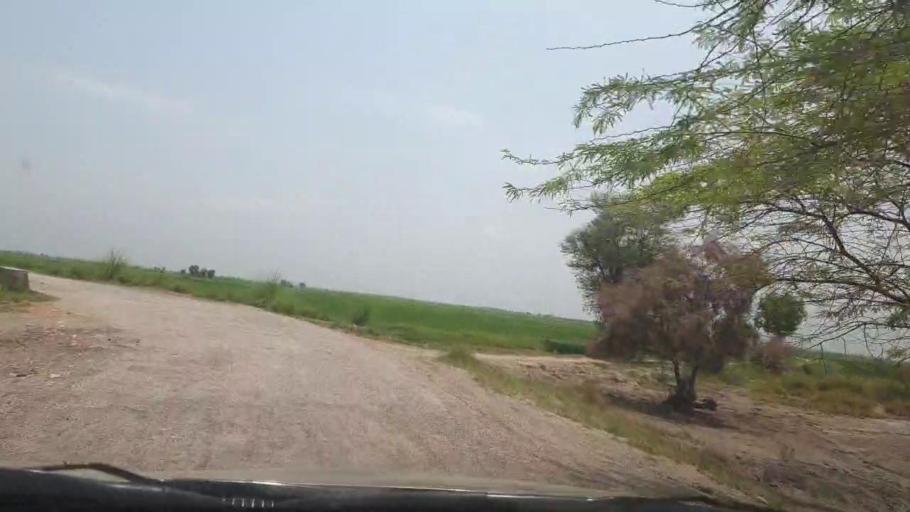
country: PK
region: Sindh
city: Ratodero
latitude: 27.7325
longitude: 68.3099
